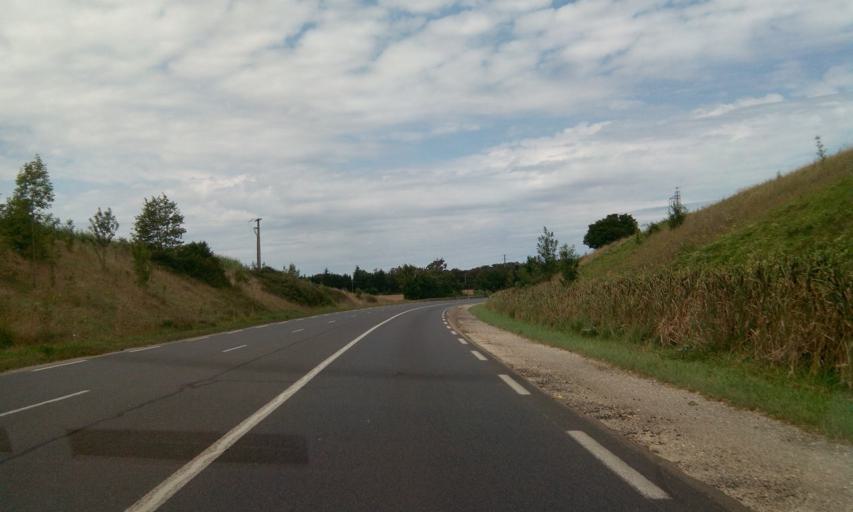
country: FR
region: Poitou-Charentes
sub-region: Departement des Deux-Sevres
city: Melle
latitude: 46.2113
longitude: -0.1542
